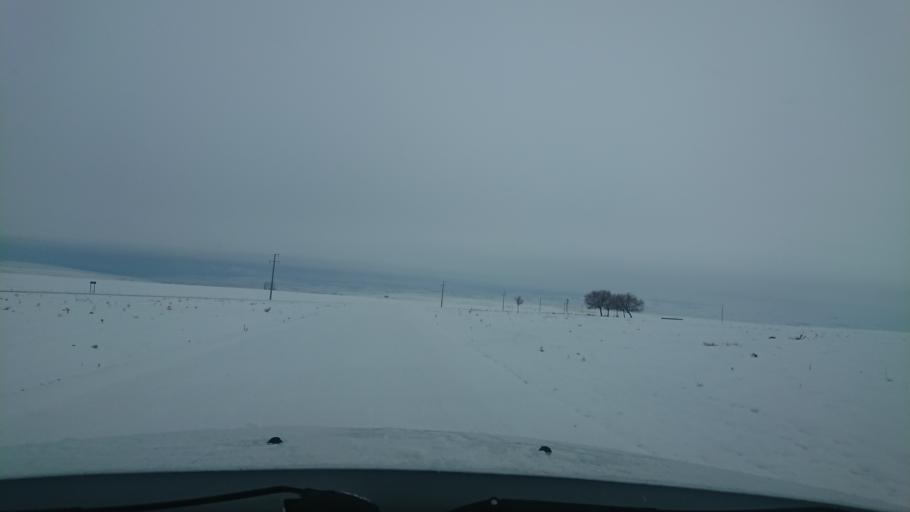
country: TR
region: Aksaray
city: Agacoren
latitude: 38.7206
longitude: 33.8667
